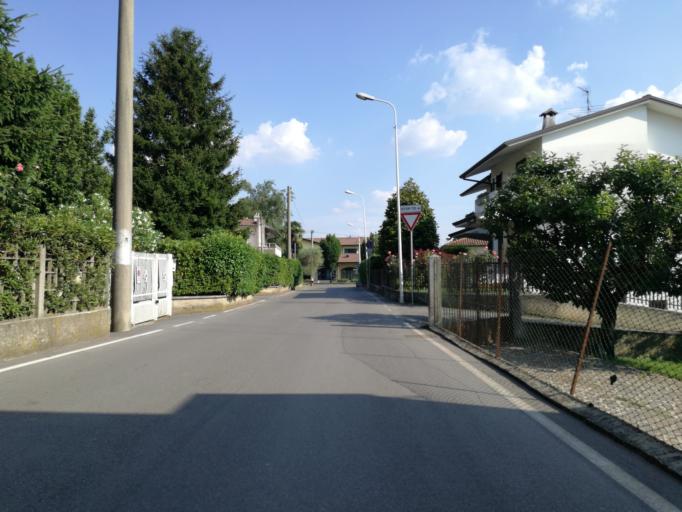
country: IT
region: Lombardy
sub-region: Provincia di Bergamo
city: Calusco d'Adda
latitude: 45.6859
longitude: 9.4585
